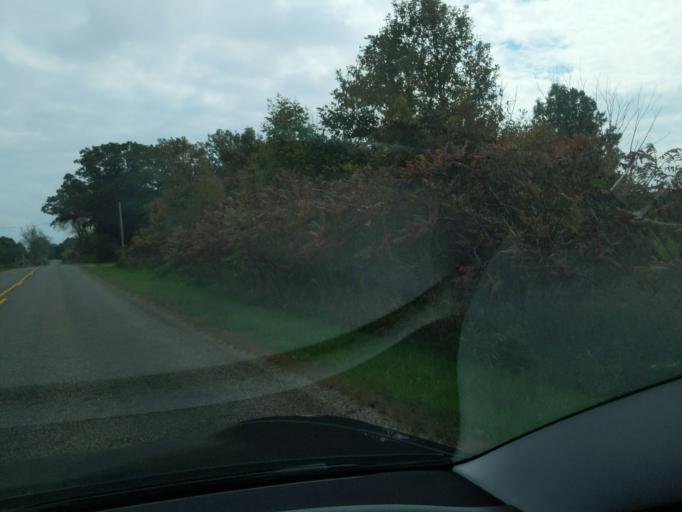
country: US
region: Michigan
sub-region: Eaton County
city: Eaton Rapids
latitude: 42.4772
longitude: -84.6303
